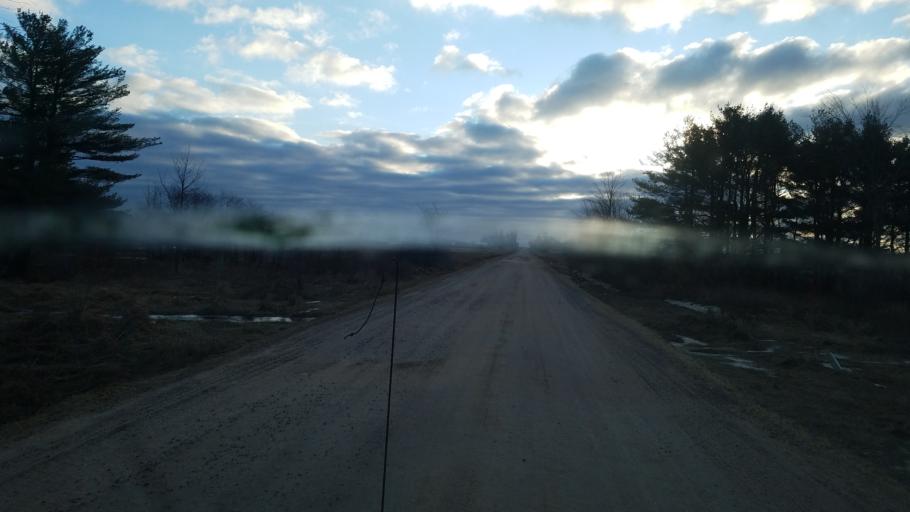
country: US
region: Wisconsin
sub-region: Clark County
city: Loyal
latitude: 44.6110
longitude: -90.4547
